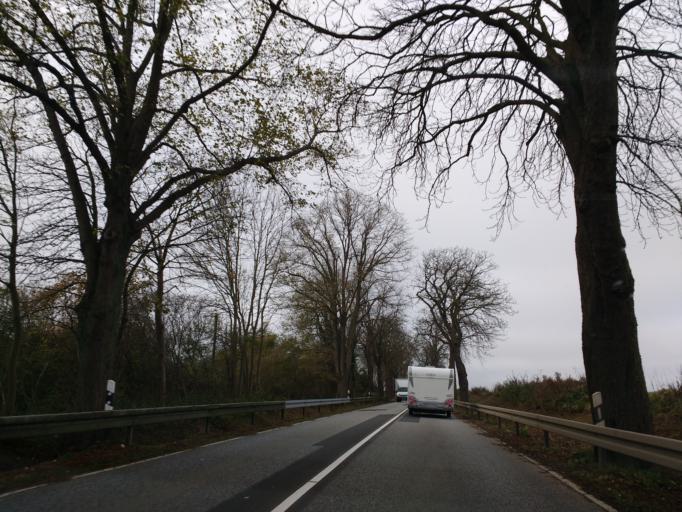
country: DE
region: Mecklenburg-Vorpommern
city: Dassow
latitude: 53.9058
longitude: 10.9584
